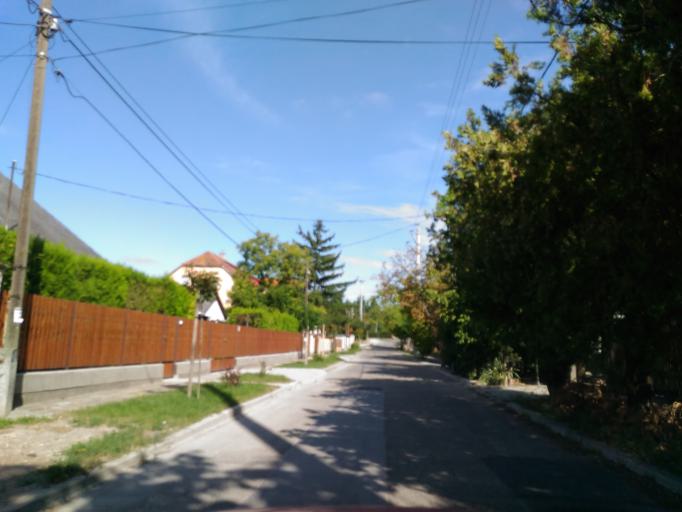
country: HU
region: Pest
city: Diosd
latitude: 47.4043
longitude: 18.9820
